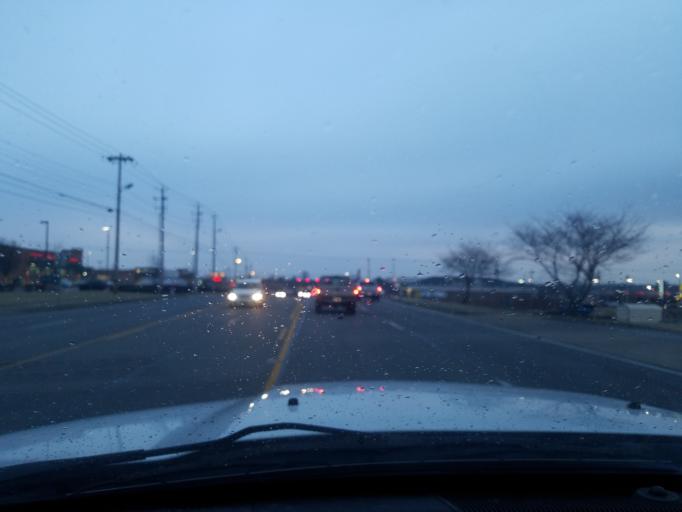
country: US
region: Kentucky
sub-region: Warren County
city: Bowling Green
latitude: 36.9629
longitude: -86.4697
